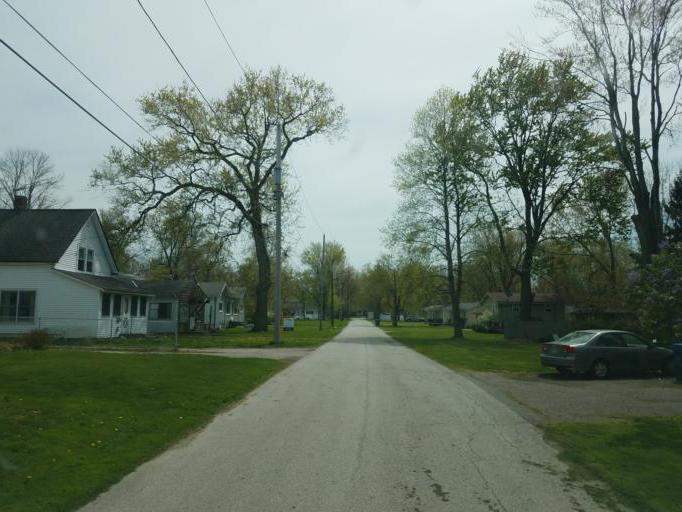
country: US
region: Ohio
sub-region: Lake County
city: Mentor-on-the-Lake
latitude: 41.7124
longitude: -81.3760
